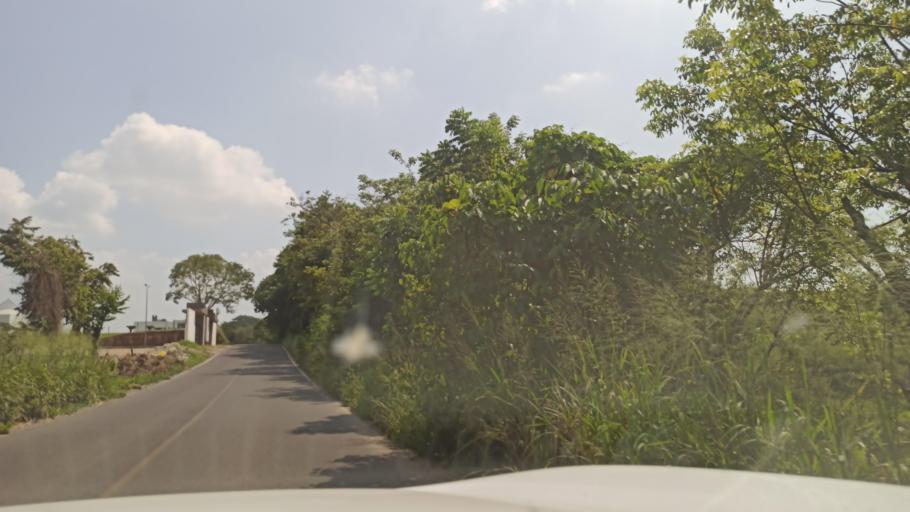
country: MX
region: Veracruz
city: Martinez de la Torre
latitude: 20.0847
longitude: -97.0761
